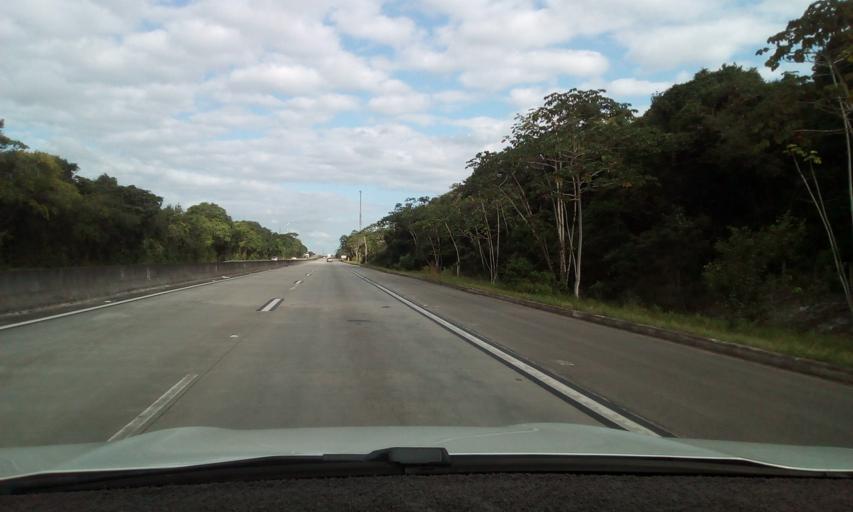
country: BR
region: Paraiba
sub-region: Mamanguape
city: Mamanguape
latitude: -6.9778
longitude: -35.0779
